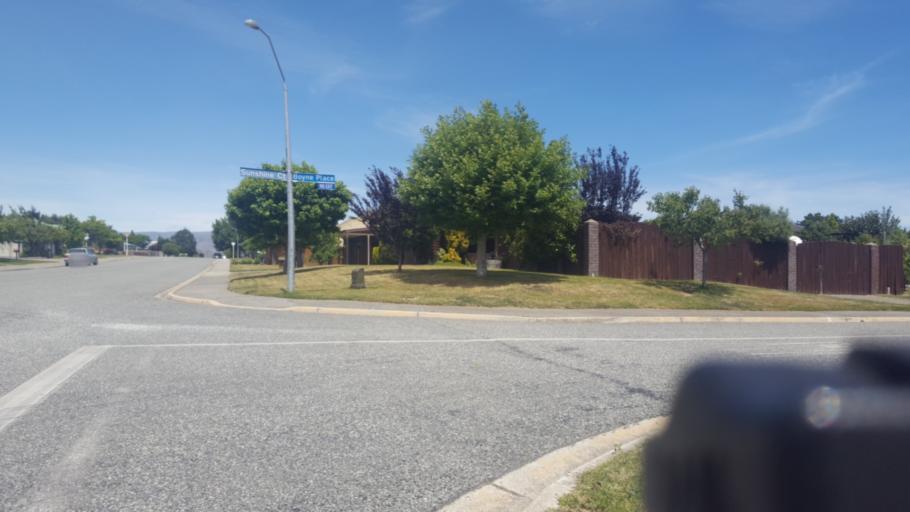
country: NZ
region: Otago
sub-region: Queenstown-Lakes District
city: Wanaka
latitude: -45.0436
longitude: 169.2008
